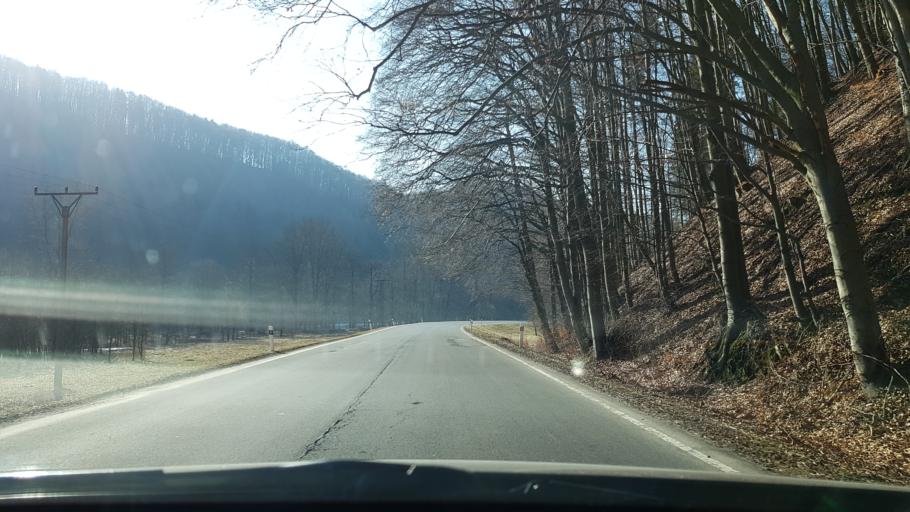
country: CZ
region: Olomoucky
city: Dolni Bohdikov
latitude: 50.0442
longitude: 16.9148
